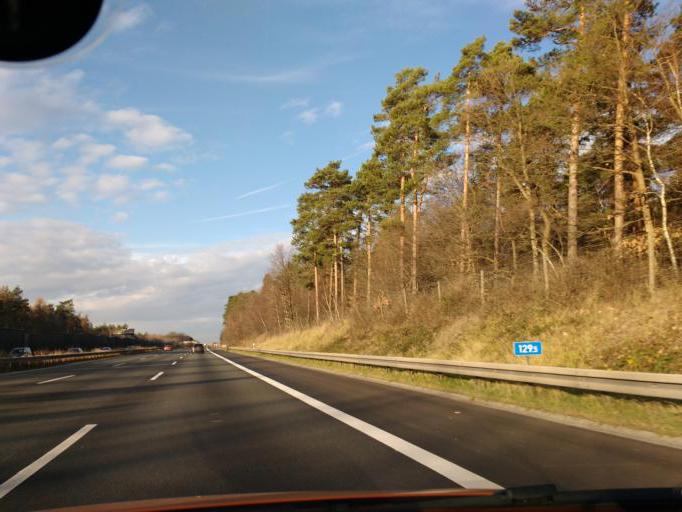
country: DE
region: Saxony-Anhalt
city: Harbke
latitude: 52.2237
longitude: 11.0466
